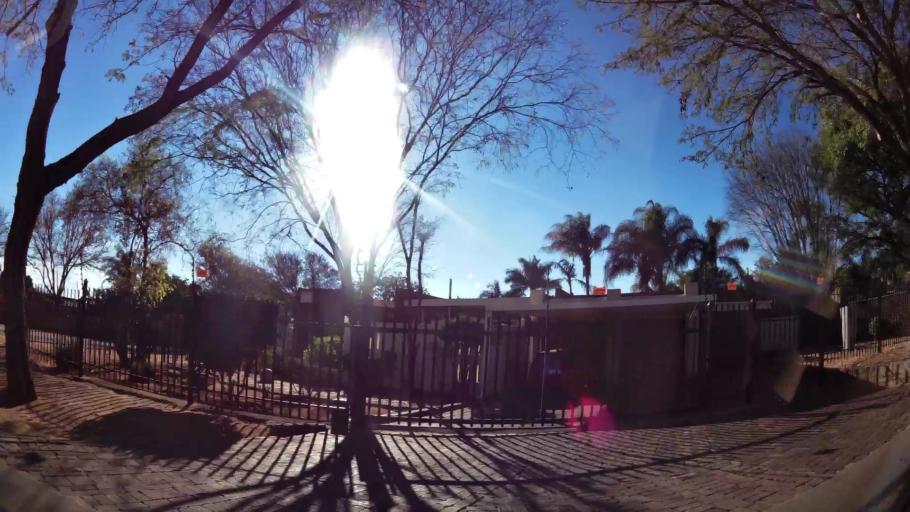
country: ZA
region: Limpopo
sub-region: Capricorn District Municipality
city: Polokwane
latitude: -23.8944
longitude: 29.4830
